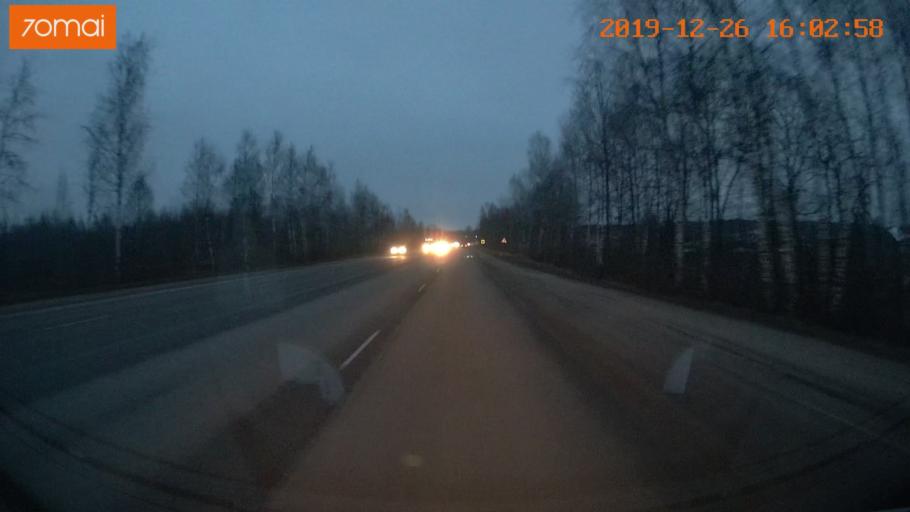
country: RU
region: Jaroslavl
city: Rybinsk
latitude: 58.0111
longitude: 38.8475
